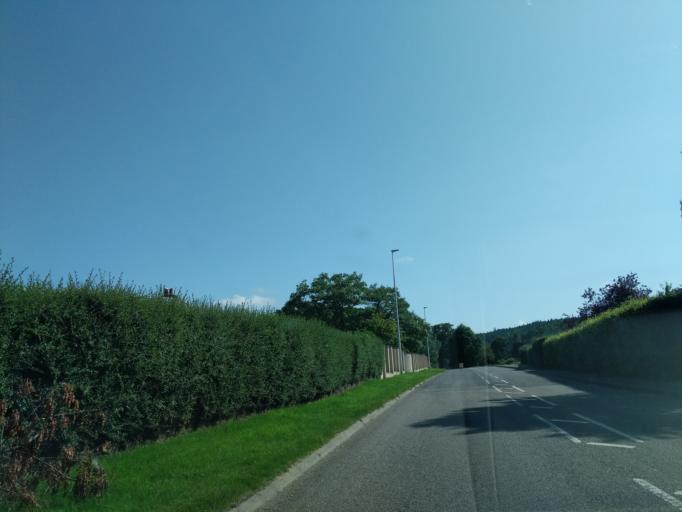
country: GB
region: Scotland
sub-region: Moray
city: Fochabers
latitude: 57.6109
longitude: -3.0891
